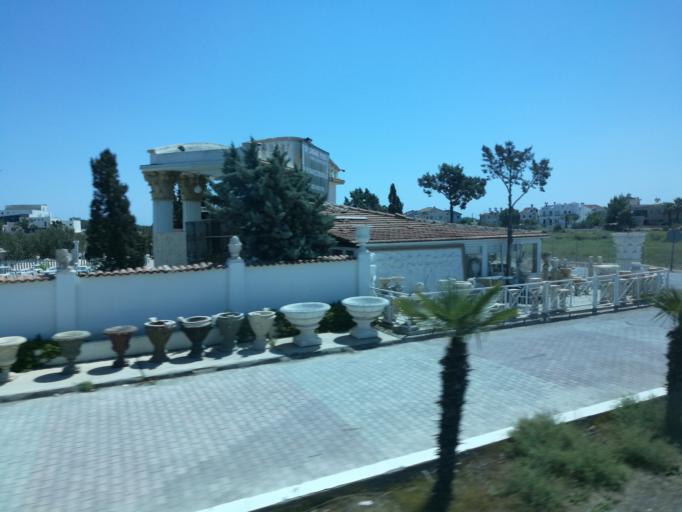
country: CY
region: Ammochostos
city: Famagusta
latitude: 35.1631
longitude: 33.9009
